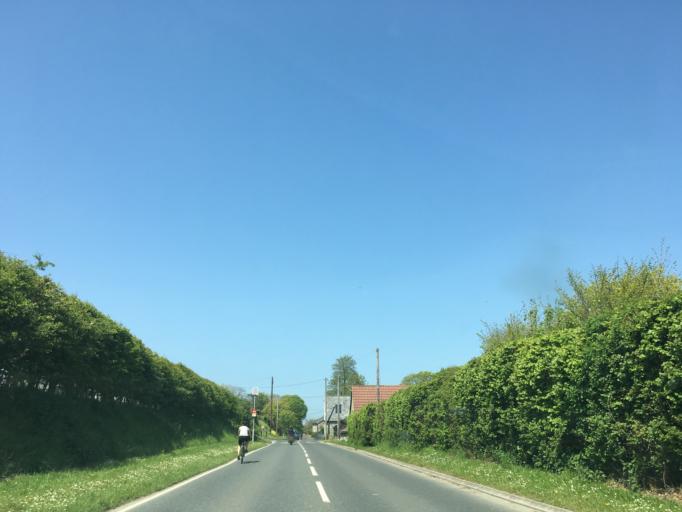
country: GB
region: England
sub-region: Isle of Wight
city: Niton
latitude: 50.5944
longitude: -1.2622
